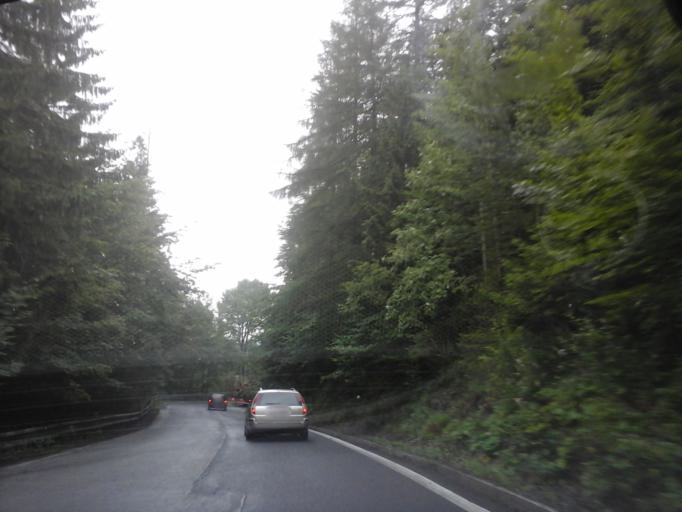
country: SK
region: Kosicky
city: Dobsina
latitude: 48.8993
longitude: 20.2488
